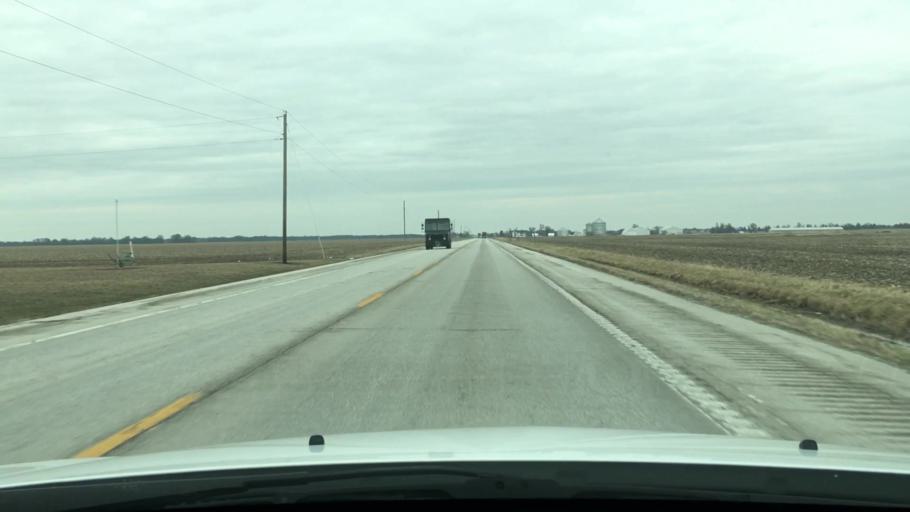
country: US
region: Missouri
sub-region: Audrain County
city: Vandalia
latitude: 39.2705
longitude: -91.6445
